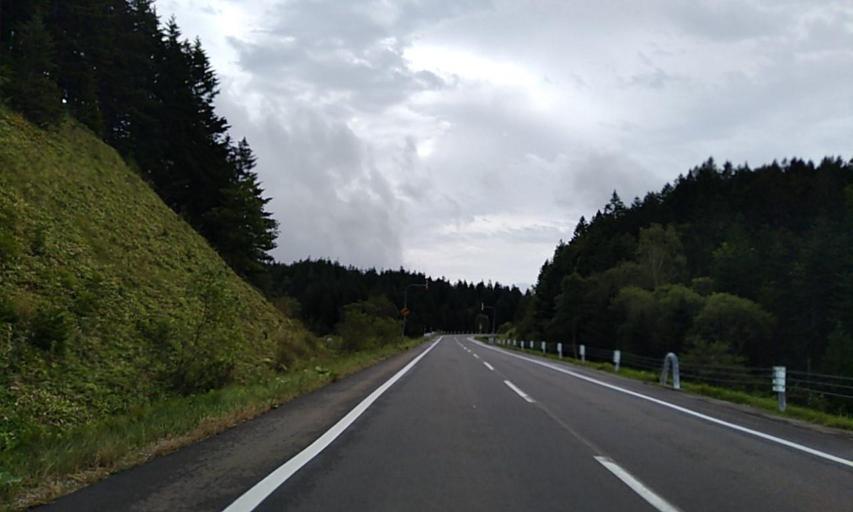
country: JP
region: Hokkaido
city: Abashiri
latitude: 43.6251
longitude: 144.5776
